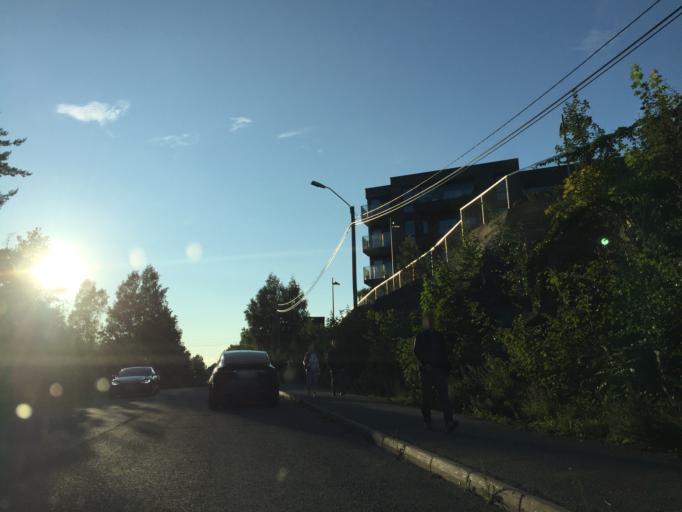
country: NO
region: Akershus
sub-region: Baerum
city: Lysaker
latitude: 59.9063
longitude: 10.6238
